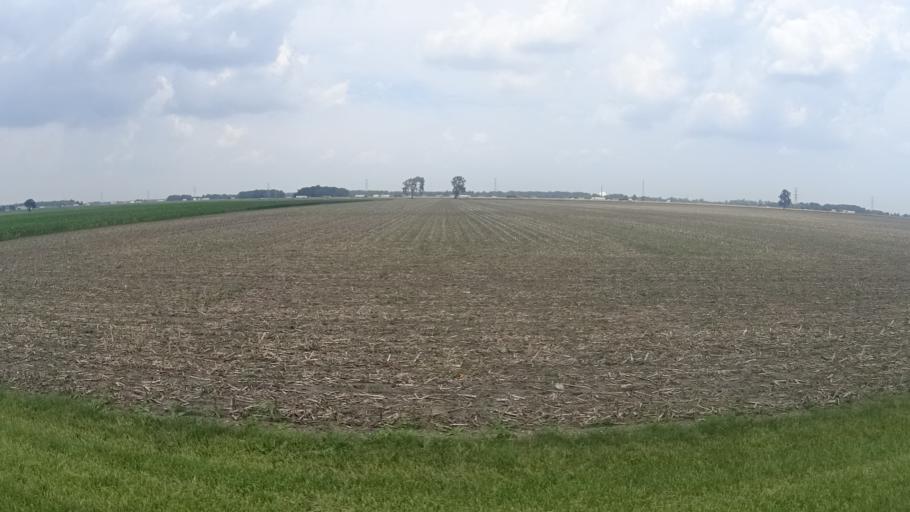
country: US
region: Ohio
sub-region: Erie County
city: Milan
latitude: 41.3229
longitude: -82.6592
